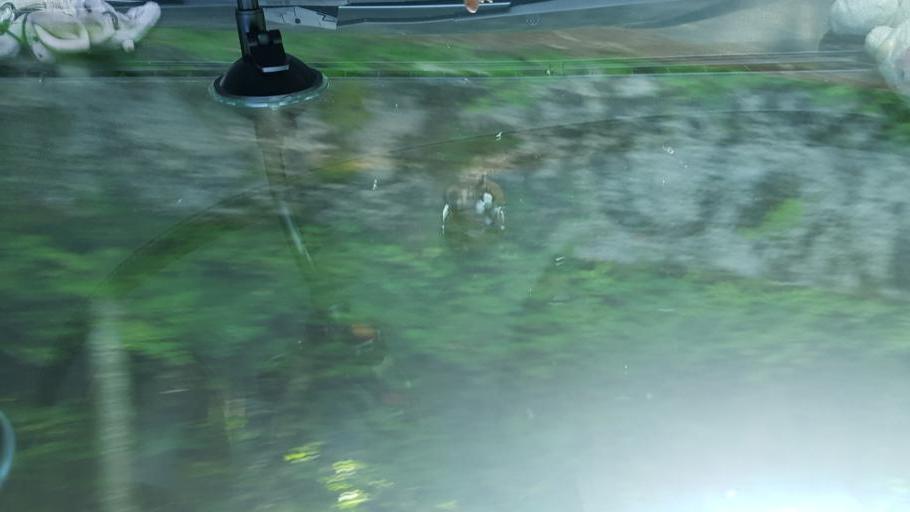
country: IT
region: Friuli Venezia Giulia
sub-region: Provincia di Udine
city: Prato
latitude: 46.3487
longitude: 13.3940
